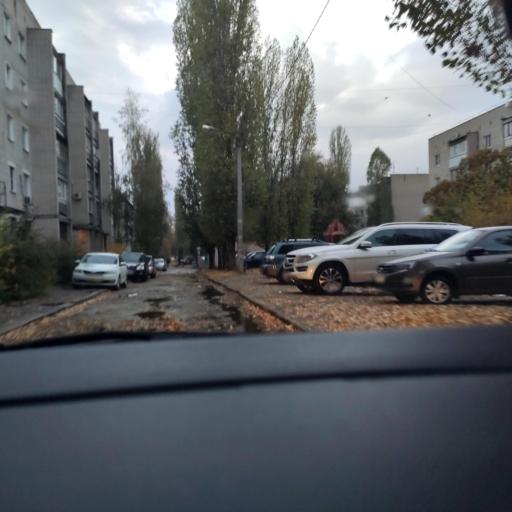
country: RU
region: Voronezj
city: Pridonskoy
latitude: 51.6561
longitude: 39.1245
